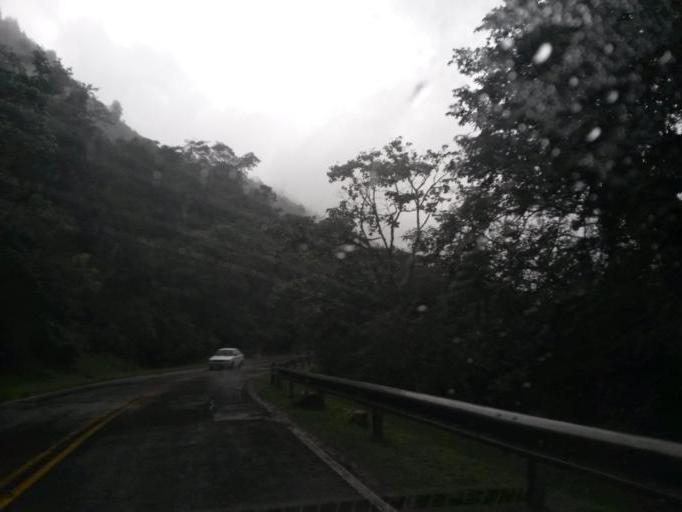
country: CO
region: Cauca
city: Popayan
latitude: 2.3730
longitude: -76.4984
